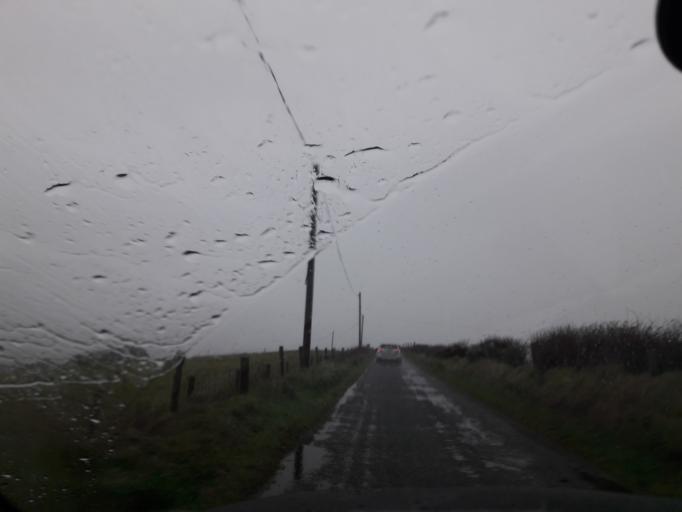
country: IE
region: Ulster
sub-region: County Donegal
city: Ramelton
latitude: 55.2675
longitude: -7.6470
